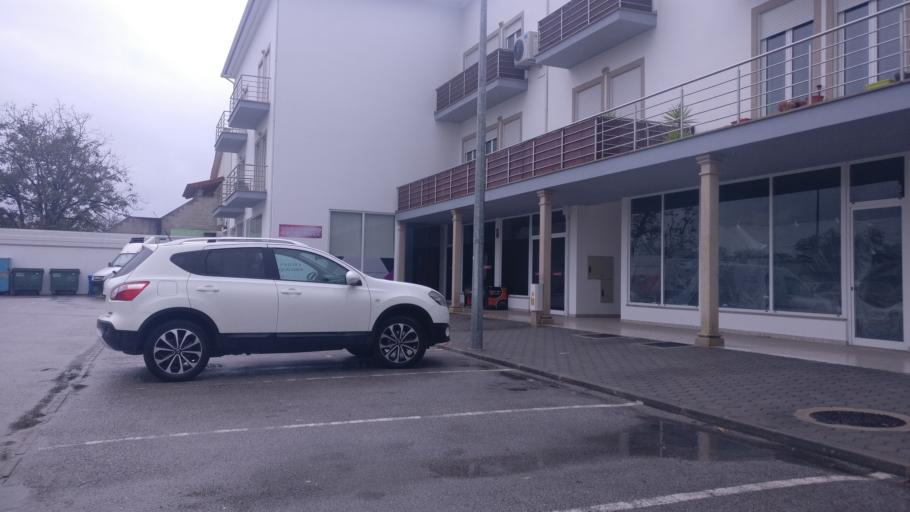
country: PT
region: Viseu
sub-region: Mortagua
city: Mortagua
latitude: 40.3964
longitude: -8.2282
